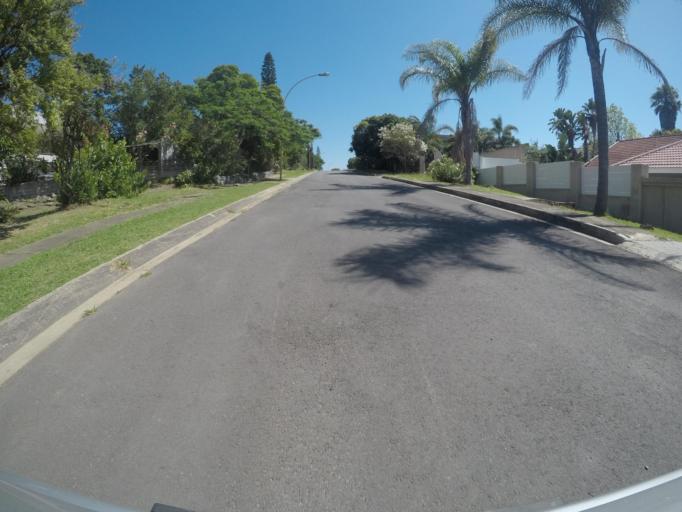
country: ZA
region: Eastern Cape
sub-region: Buffalo City Metropolitan Municipality
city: East London
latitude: -32.9720
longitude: 27.9197
